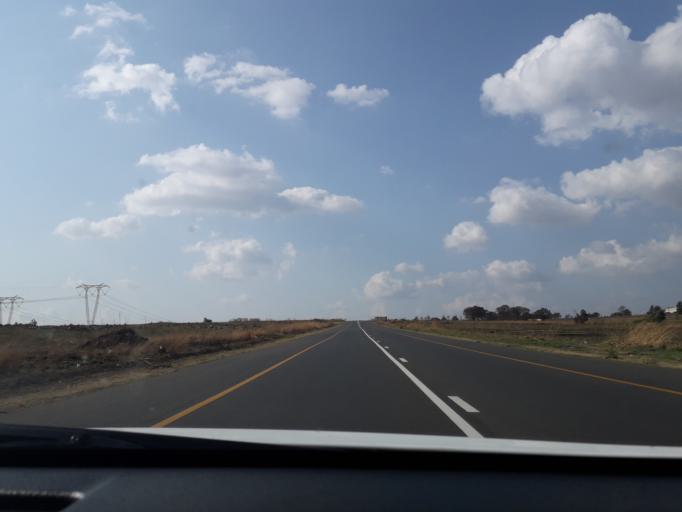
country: ZA
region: Gauteng
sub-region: City of Tshwane Metropolitan Municipality
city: Centurion
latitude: -25.9098
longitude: 28.2467
